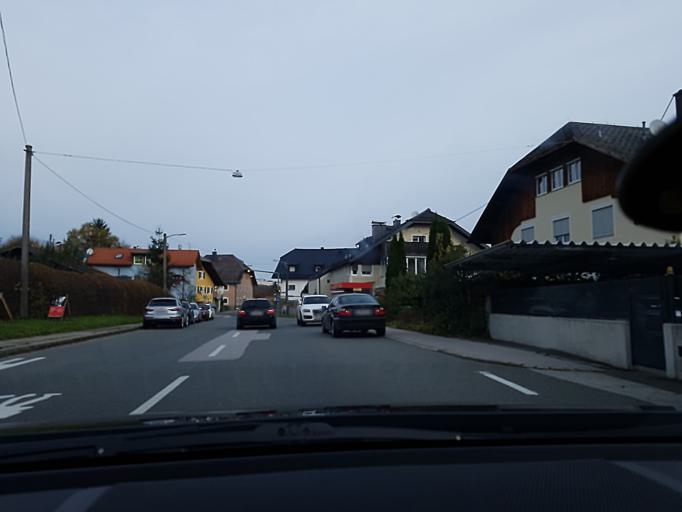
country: AT
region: Salzburg
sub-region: Politischer Bezirk Salzburg-Umgebung
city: Anif
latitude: 47.7697
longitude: 13.0584
